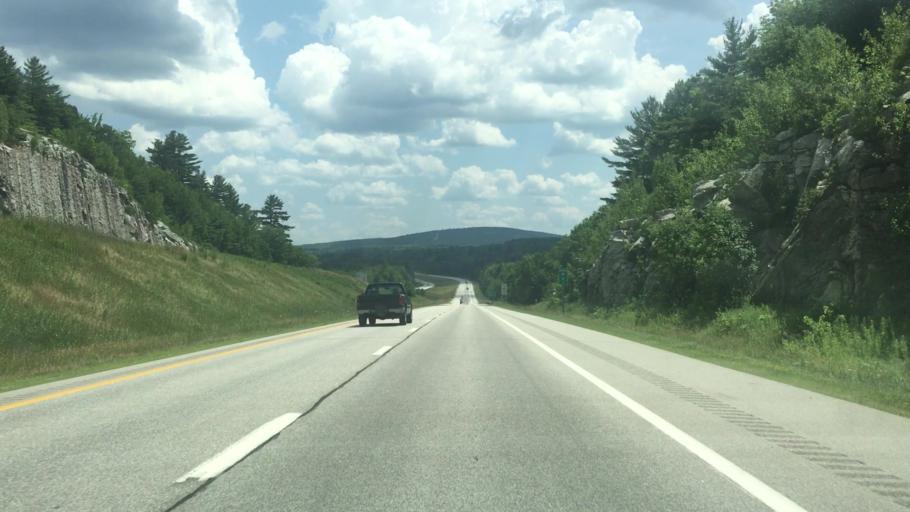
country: US
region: New Hampshire
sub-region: Merrimack County
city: New London
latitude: 43.4140
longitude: -72.0304
